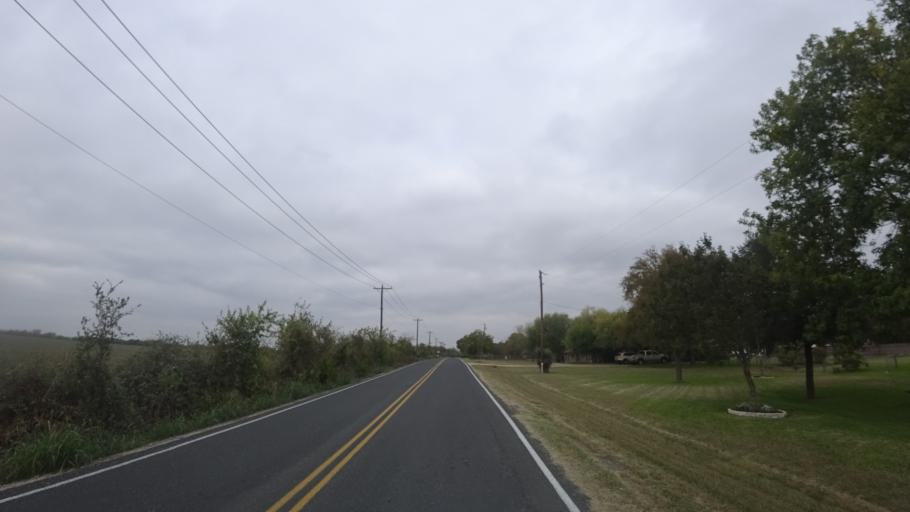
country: US
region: Texas
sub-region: Travis County
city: Pflugerville
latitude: 30.3941
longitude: -97.5963
